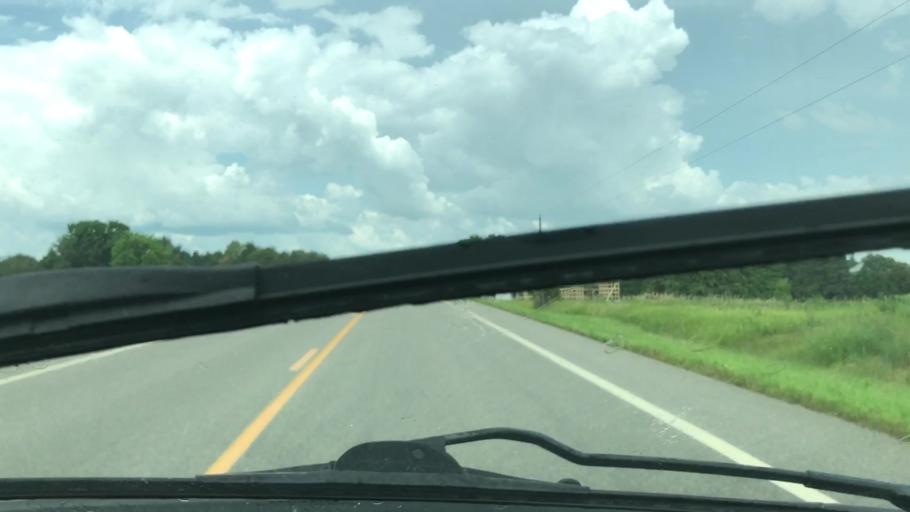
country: US
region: Minnesota
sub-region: Olmsted County
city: Stewartville
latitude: 43.8725
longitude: -92.5286
